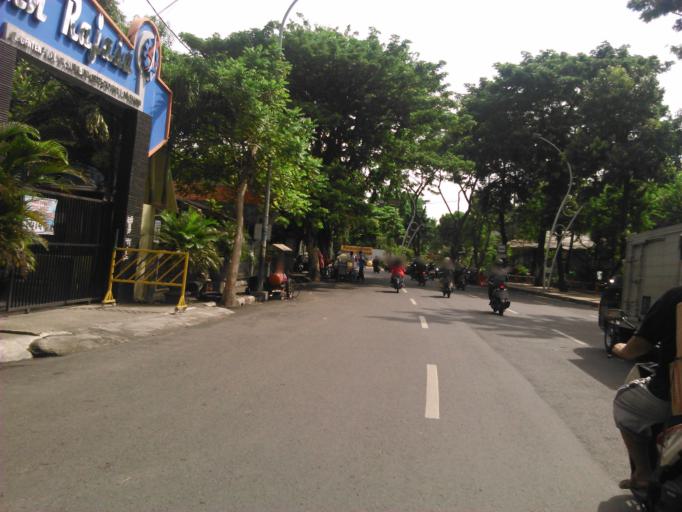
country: ID
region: East Java
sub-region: Kota Surabaya
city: Surabaya
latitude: -7.2581
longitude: 112.7436
